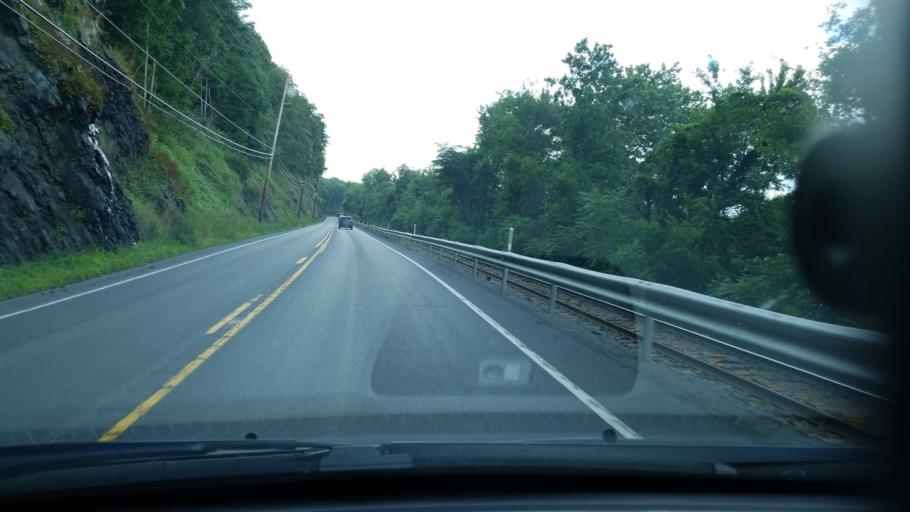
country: US
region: Pennsylvania
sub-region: Montour County
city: Danville
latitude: 40.9455
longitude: -76.6093
